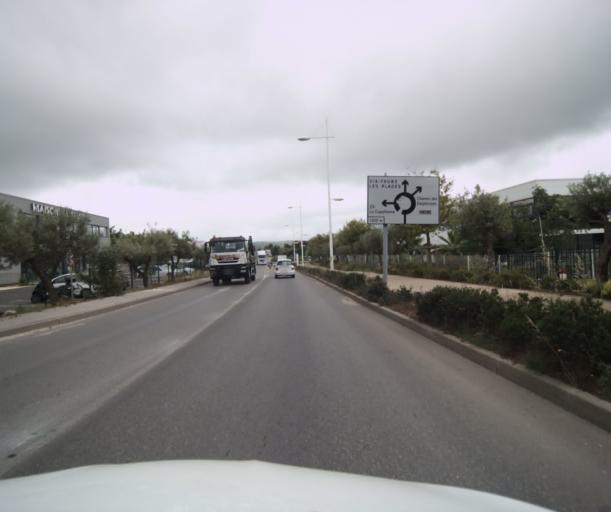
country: FR
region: Provence-Alpes-Cote d'Azur
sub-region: Departement du Var
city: Ollioules
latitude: 43.1227
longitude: 5.8475
